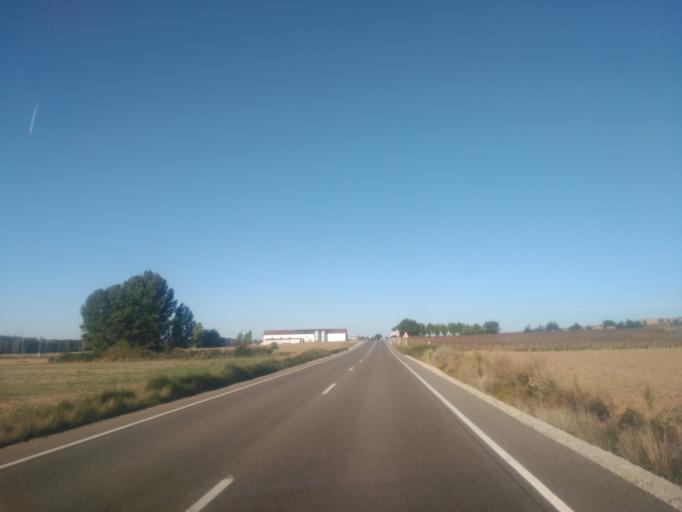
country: ES
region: Castille and Leon
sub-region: Provincia de Burgos
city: San Juan del Monte
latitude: 41.6905
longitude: -3.5161
